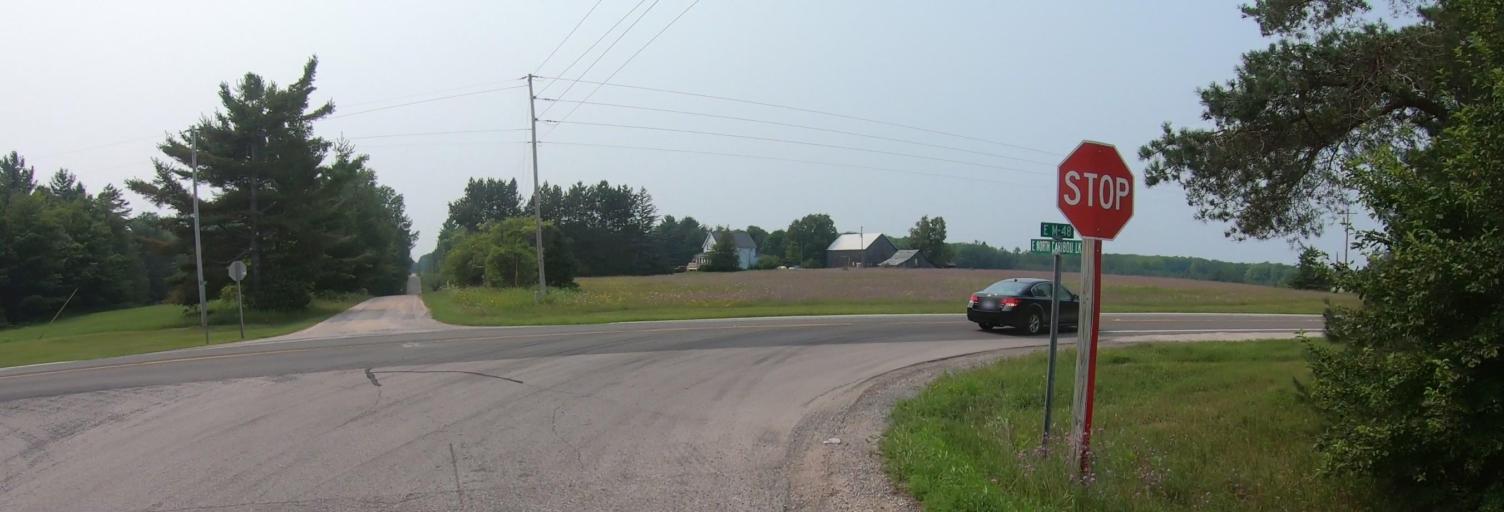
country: US
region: Michigan
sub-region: Cheboygan County
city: Cheboygan
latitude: 46.0143
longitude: -84.0711
